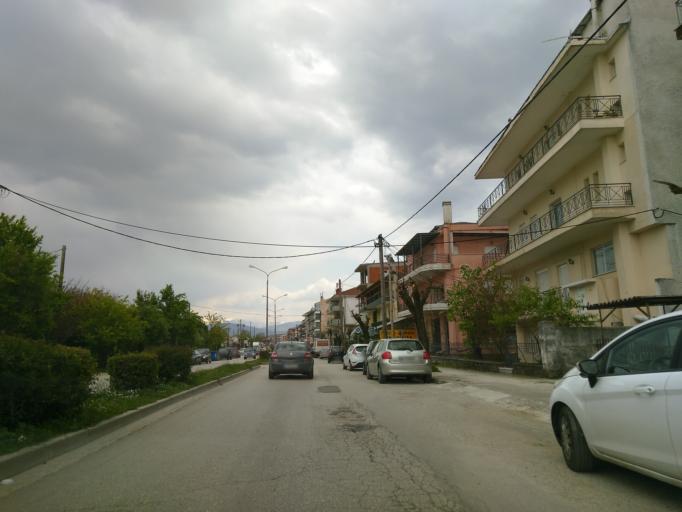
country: GR
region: Epirus
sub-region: Nomos Ioanninon
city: Ioannina
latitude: 39.6761
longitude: 20.8435
